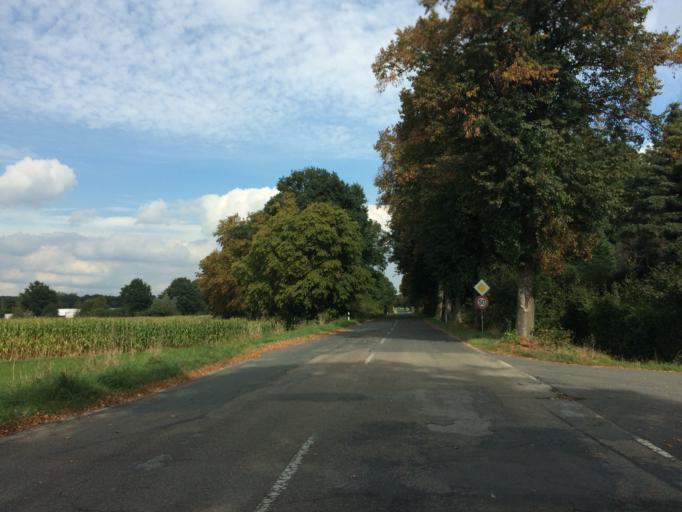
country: DE
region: North Rhine-Westphalia
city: Marl
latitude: 51.7036
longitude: 7.0917
